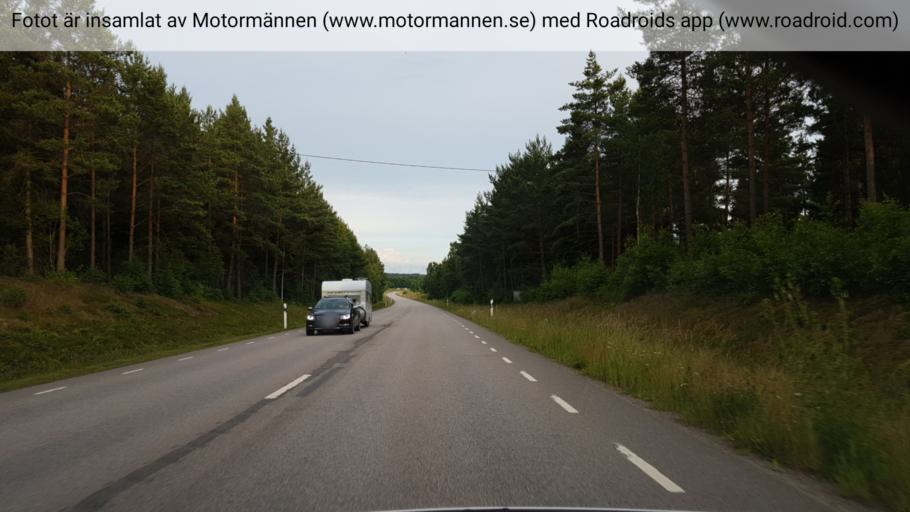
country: SE
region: Vaestra Goetaland
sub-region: Falkopings Kommun
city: Falkoeping
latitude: 58.2571
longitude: 13.5036
